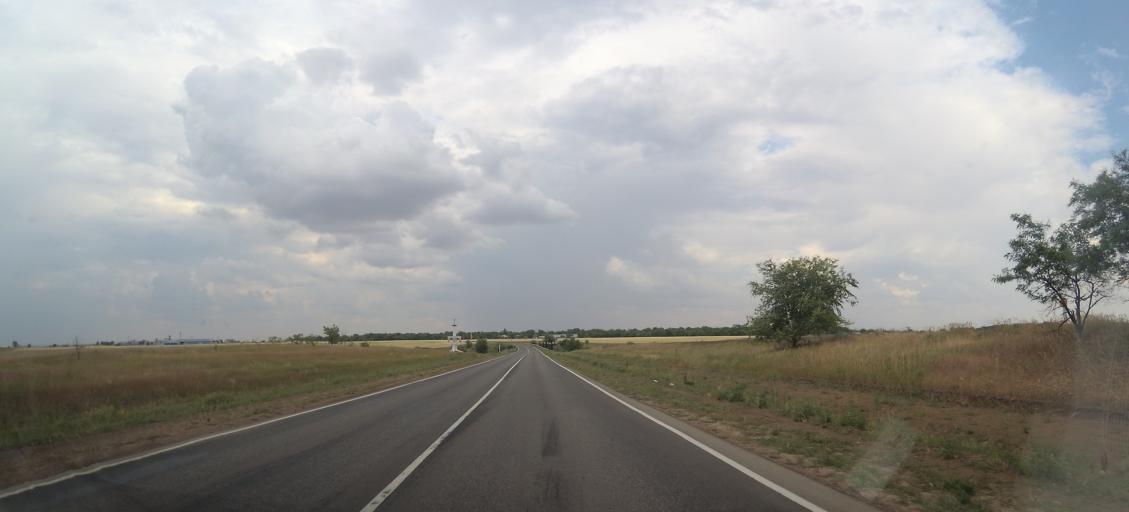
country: RU
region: Rostov
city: Sal'sk
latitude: 46.3450
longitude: 41.4207
